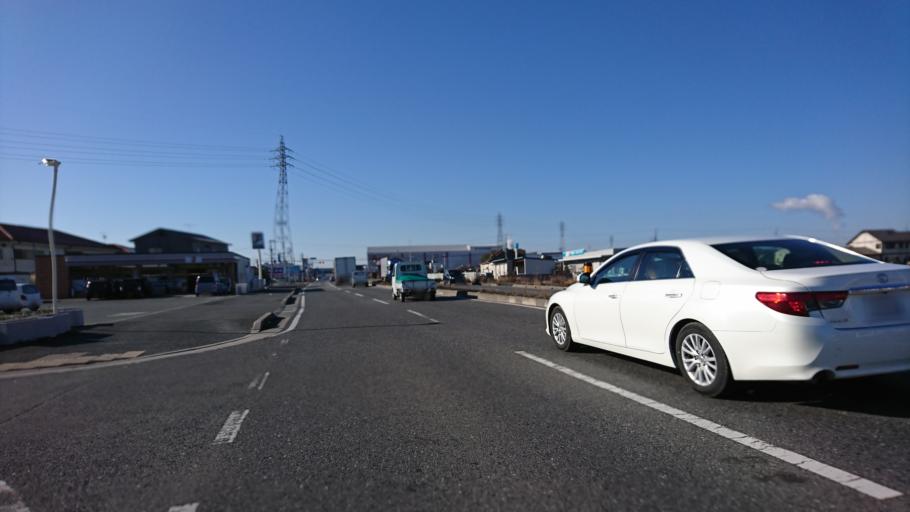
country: JP
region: Hyogo
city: Kakogawacho-honmachi
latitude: 34.7913
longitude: 134.8231
